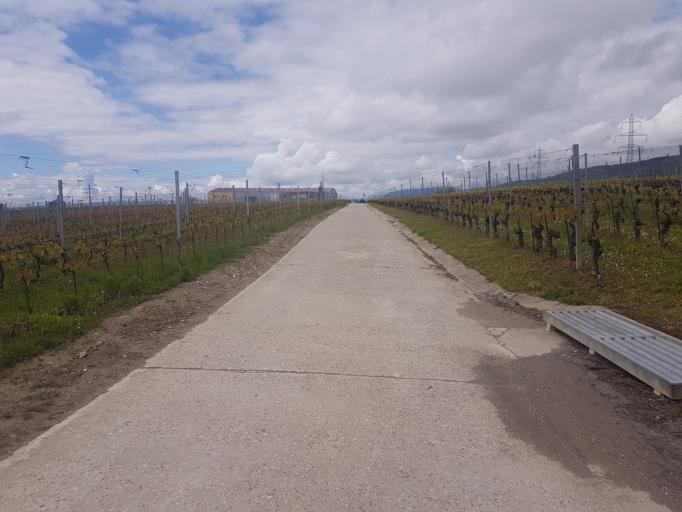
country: CH
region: Vaud
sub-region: Nyon District
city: Perroy
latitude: 46.4685
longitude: 6.3497
